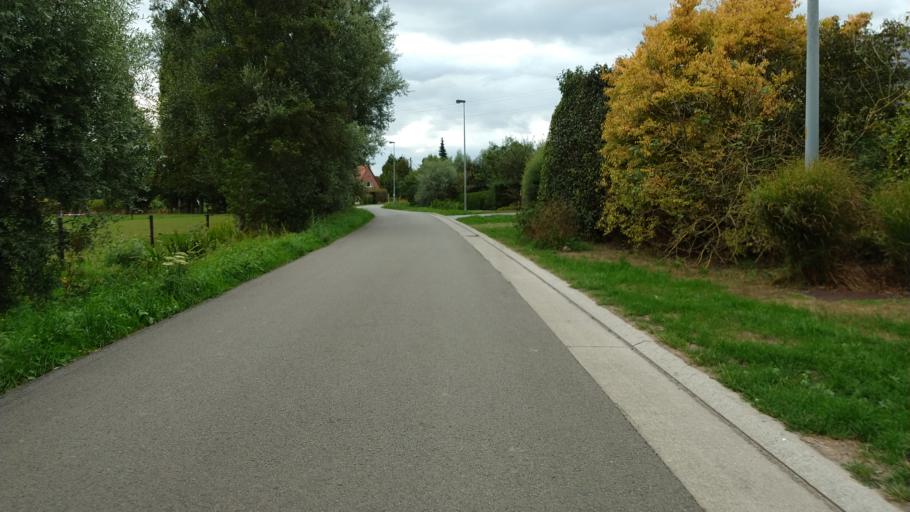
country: BE
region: Flanders
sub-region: Provincie Oost-Vlaanderen
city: Sint-Martens-Latem
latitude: 51.0579
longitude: 3.6296
